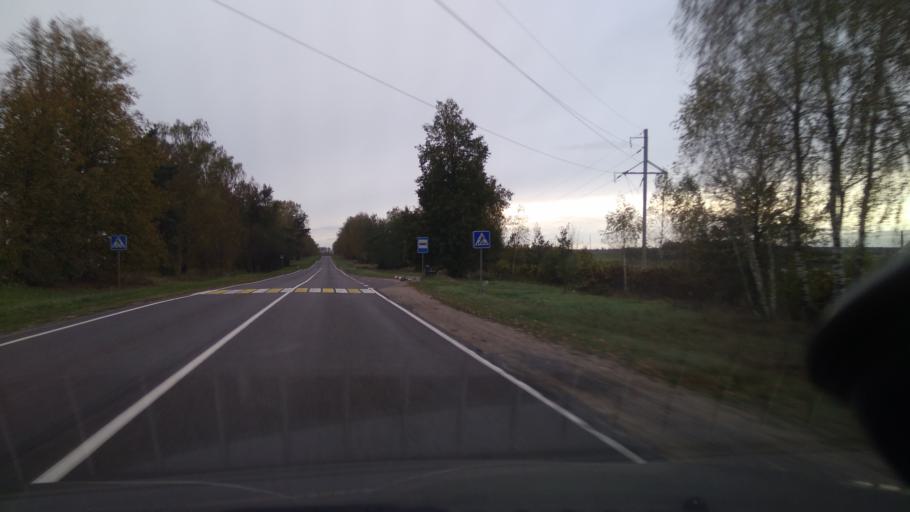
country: BY
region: Minsk
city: Rudzyensk
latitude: 53.6239
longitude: 27.8671
